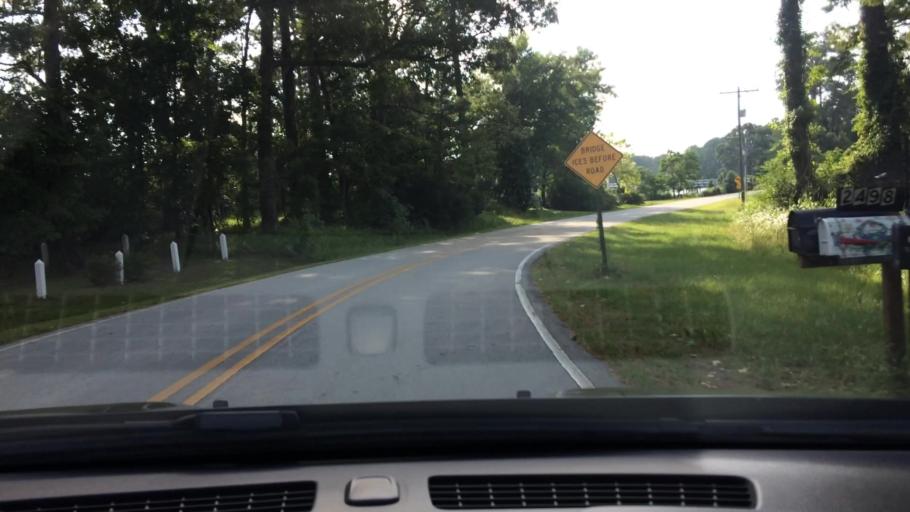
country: US
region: North Carolina
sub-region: Beaufort County
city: River Road
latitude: 35.4323
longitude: -76.9680
